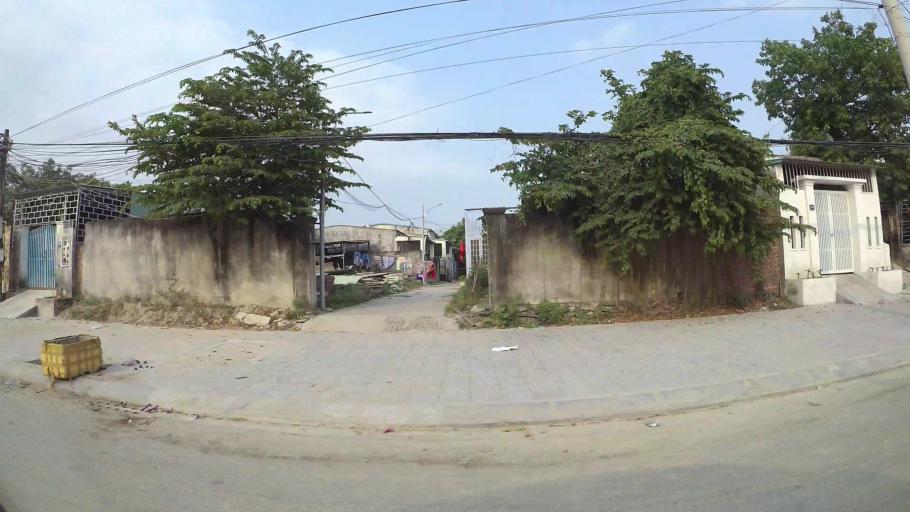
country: VN
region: Da Nang
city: Lien Chieu
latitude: 16.0486
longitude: 108.1561
